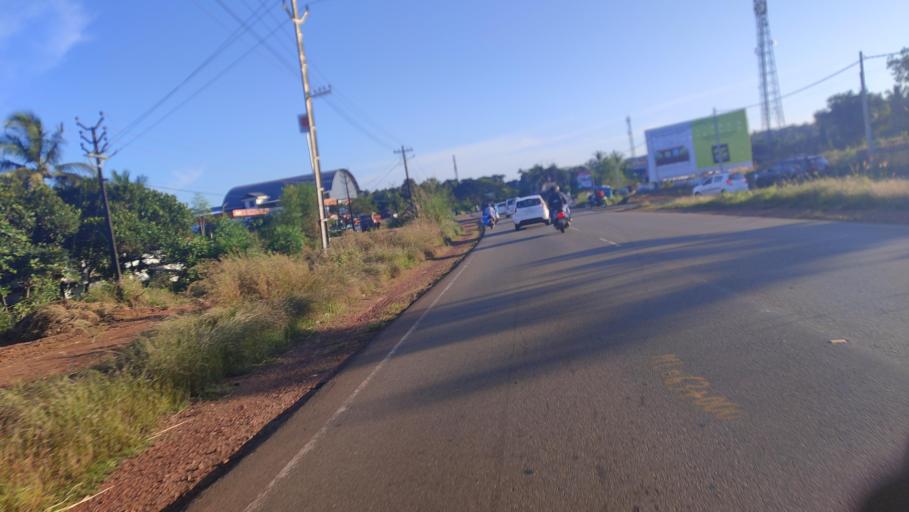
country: IN
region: Kerala
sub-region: Kasaragod District
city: Kasaragod
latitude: 12.4693
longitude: 75.0579
